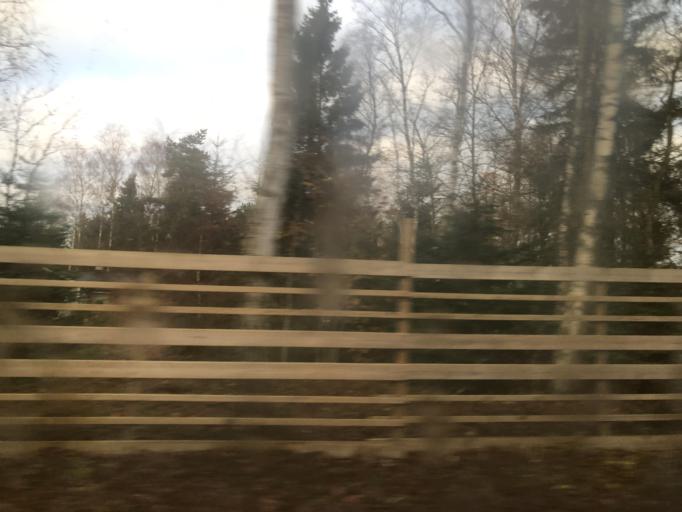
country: SE
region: Skane
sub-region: Sjobo Kommun
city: Blentarp
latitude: 55.6163
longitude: 13.5476
